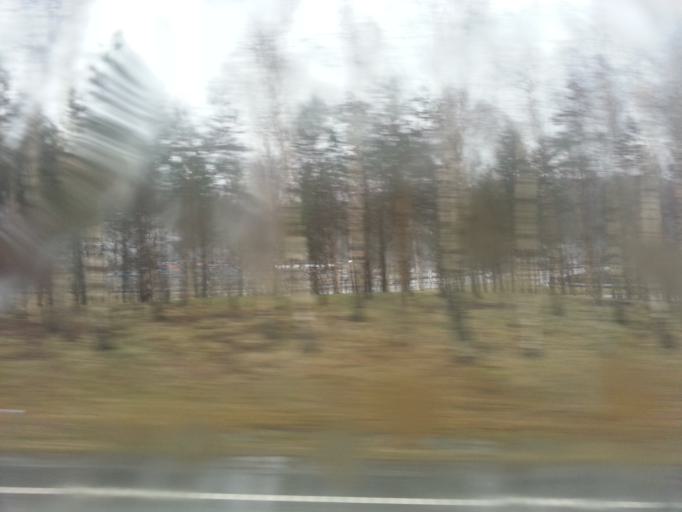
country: NO
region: Nord-Trondelag
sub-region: Stjordal
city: Stjordal
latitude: 63.4515
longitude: 10.9072
